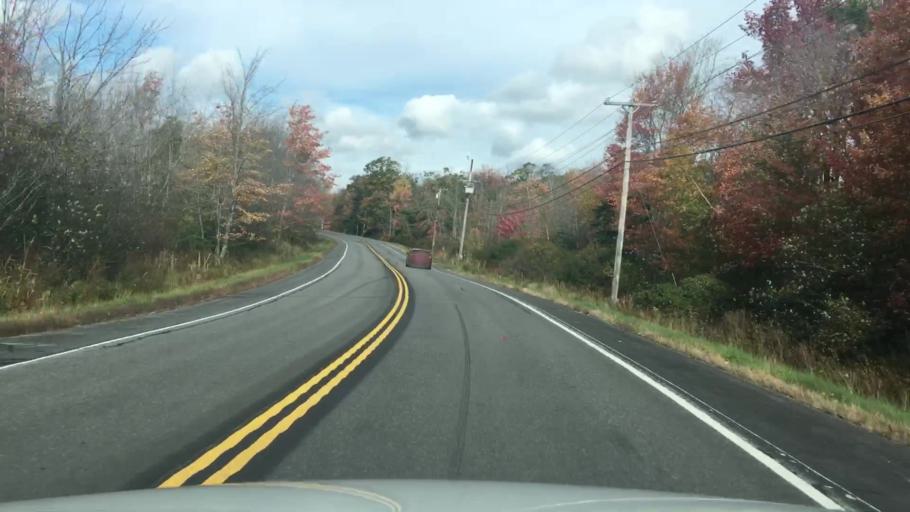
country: US
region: Maine
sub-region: Knox County
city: Rockport
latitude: 44.1721
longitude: -69.1206
